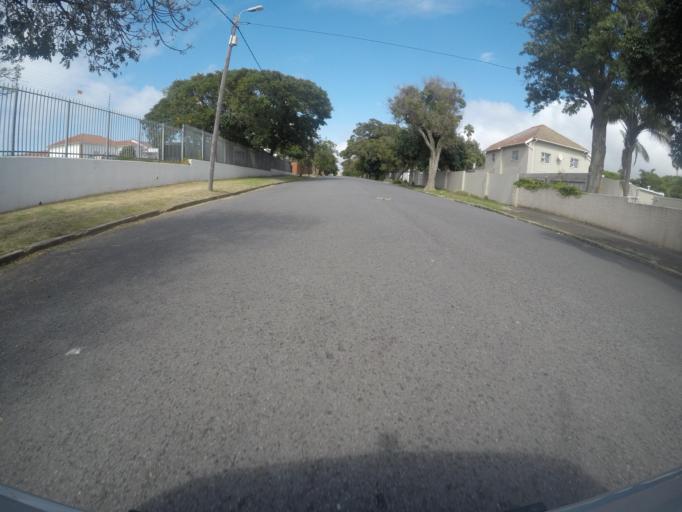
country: ZA
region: Eastern Cape
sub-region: Buffalo City Metropolitan Municipality
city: East London
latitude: -32.9930
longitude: 27.9005
